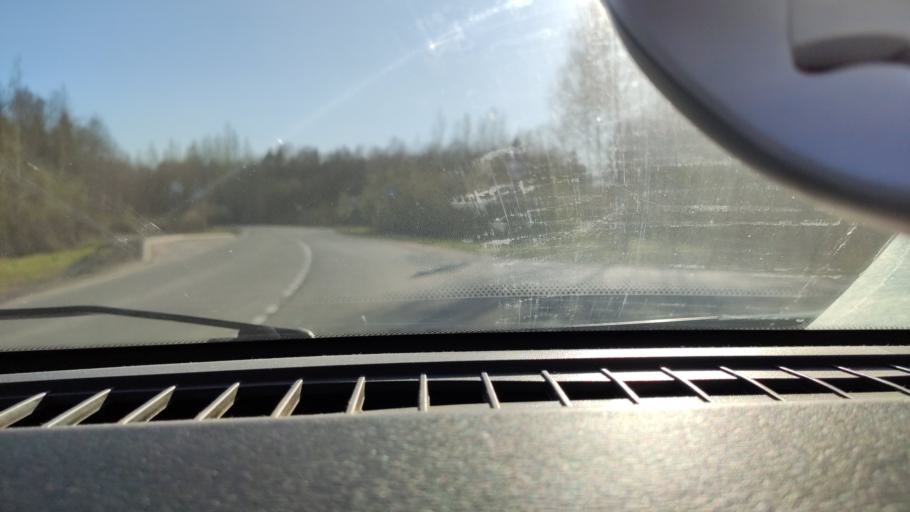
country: RU
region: Perm
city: Polazna
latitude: 58.1239
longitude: 56.4363
